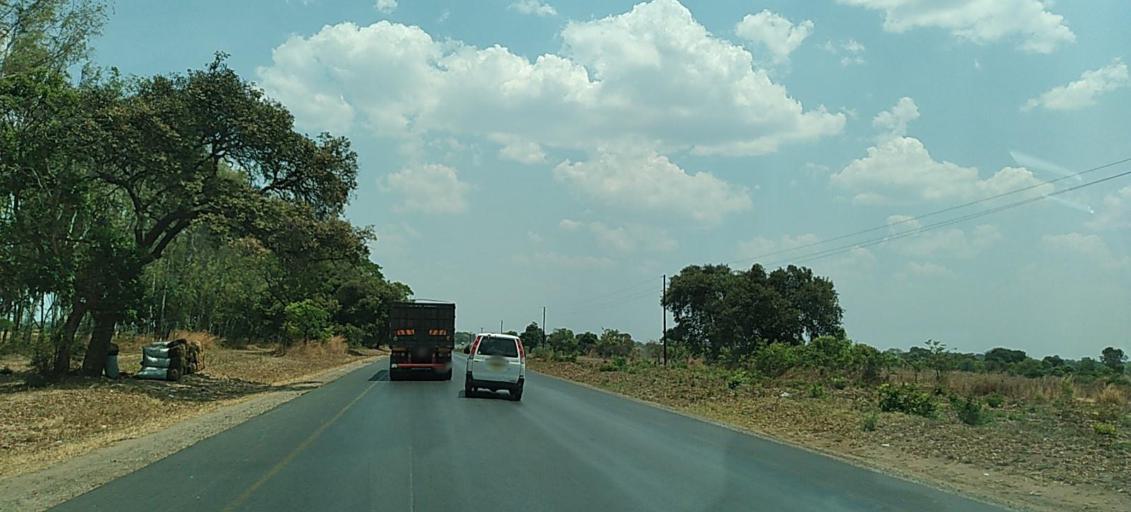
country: ZM
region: Central
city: Kabwe
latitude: -14.2346
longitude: 28.5704
